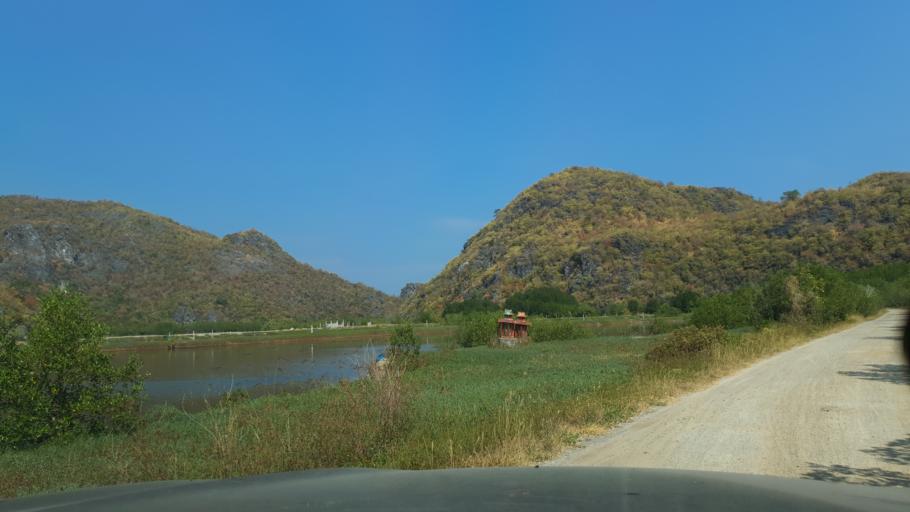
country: TH
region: Prachuap Khiri Khan
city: Sam Roi Yot
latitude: 12.1977
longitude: 99.9914
